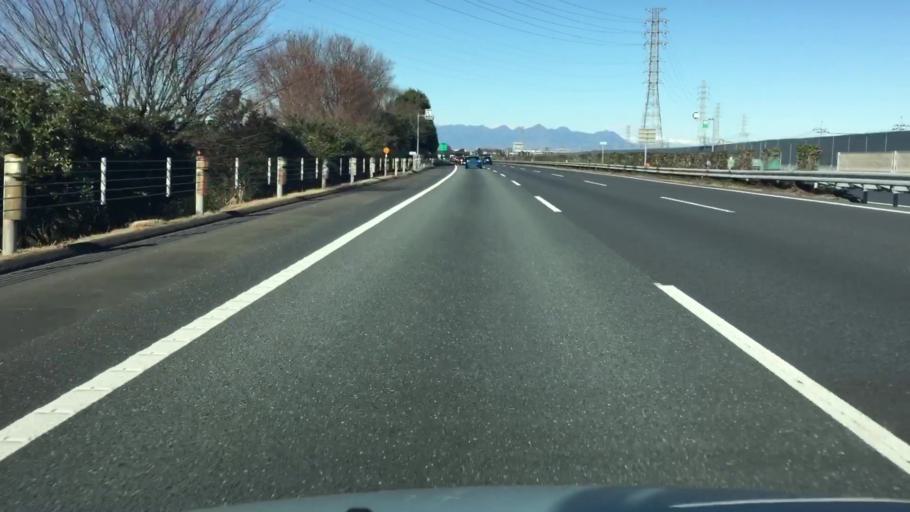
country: JP
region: Saitama
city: Honjo
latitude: 36.2244
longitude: 139.1589
